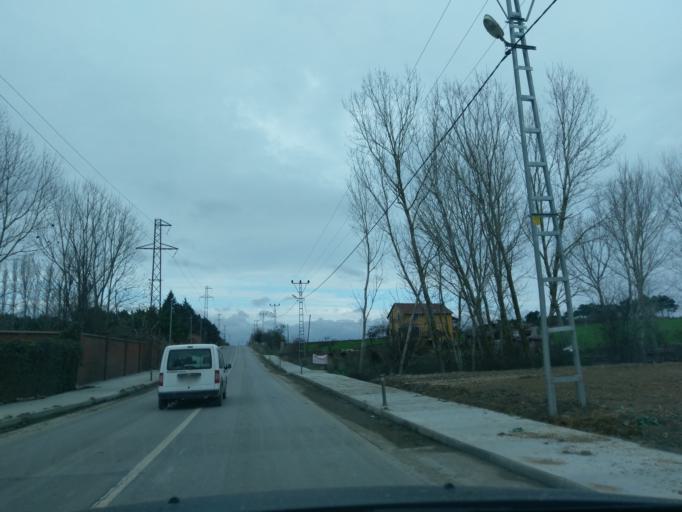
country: TR
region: Istanbul
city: Catalca
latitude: 41.1922
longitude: 28.3991
